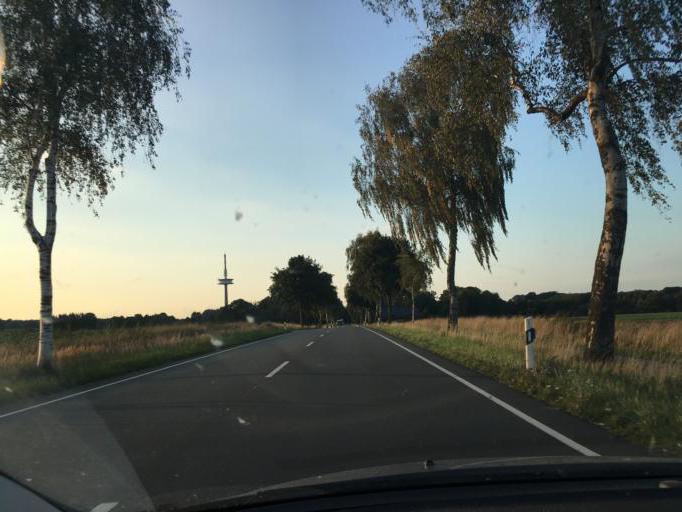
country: DE
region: Lower Saxony
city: Bergen
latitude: 52.8427
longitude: 9.9168
